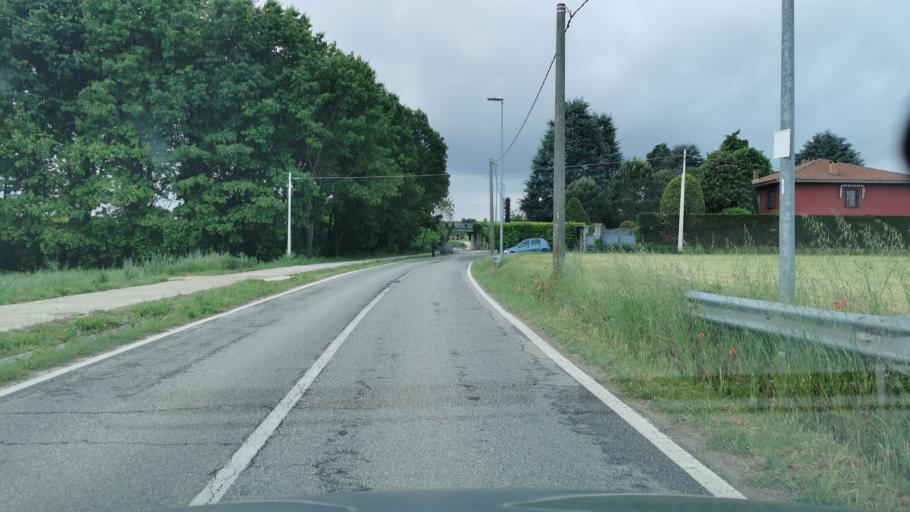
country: IT
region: Piedmont
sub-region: Provincia di Torino
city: Cambiano
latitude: 44.9952
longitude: 7.7829
